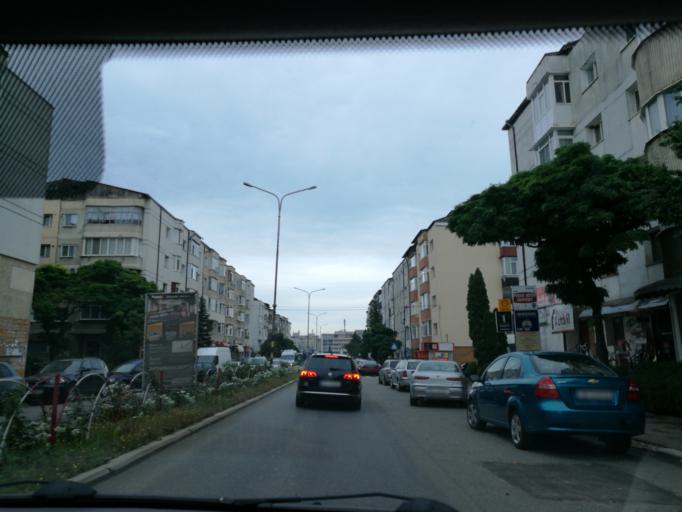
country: RO
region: Suceava
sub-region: Municipiul Falticeni
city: Falticeni
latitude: 47.4554
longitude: 26.2979
